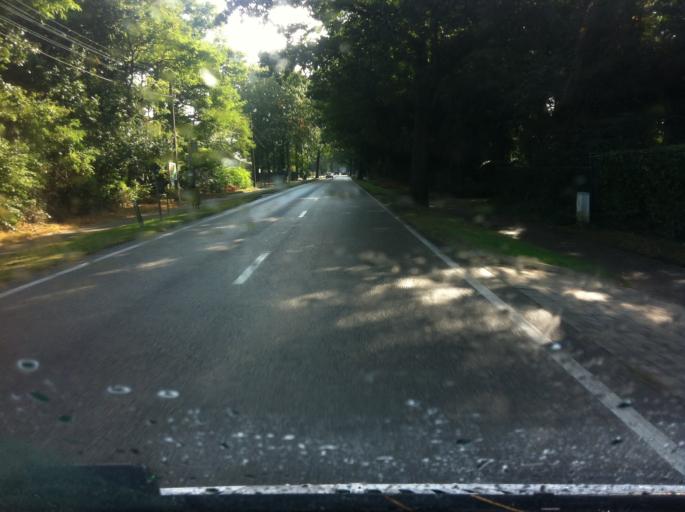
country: BE
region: Flanders
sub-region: Provincie Limburg
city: Maasmechelen
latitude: 50.9767
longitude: 5.6652
